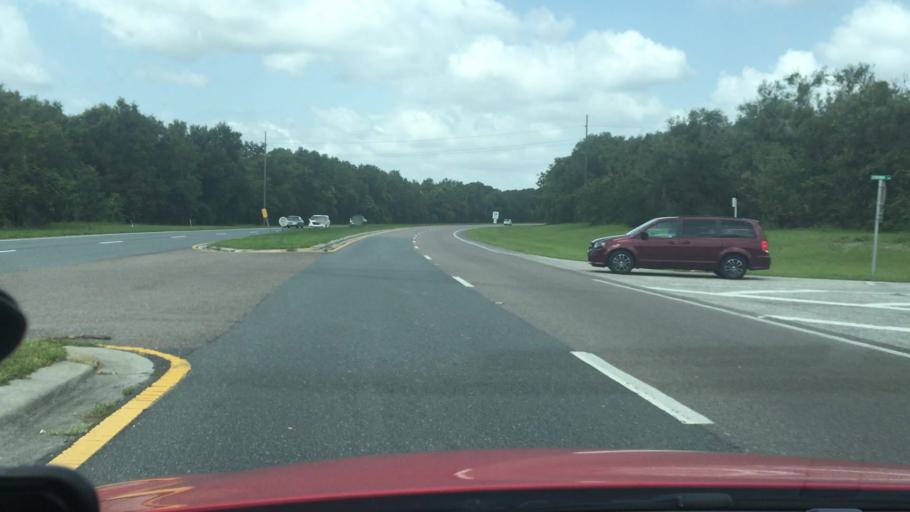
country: US
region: Florida
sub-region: Volusia County
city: Lake Helen
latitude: 29.0160
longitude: -81.2392
